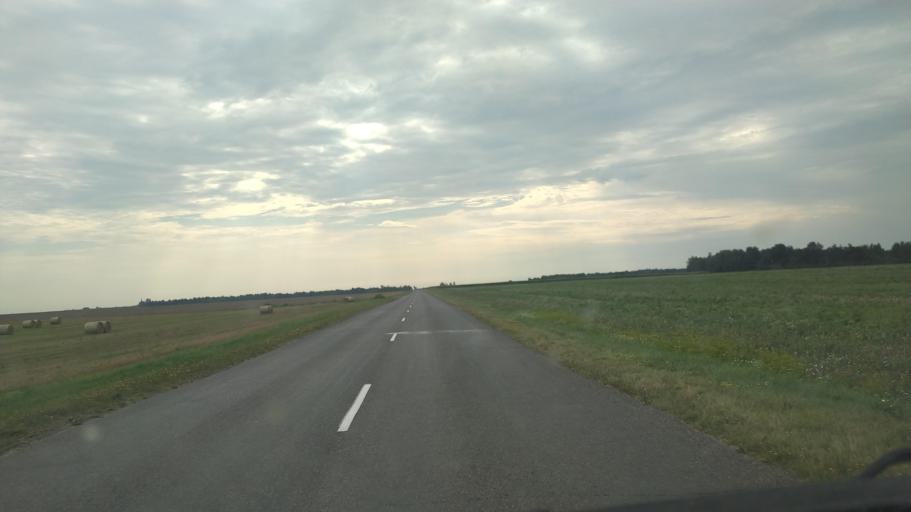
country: BY
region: Brest
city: Byaroza
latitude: 52.5732
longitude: 24.8814
